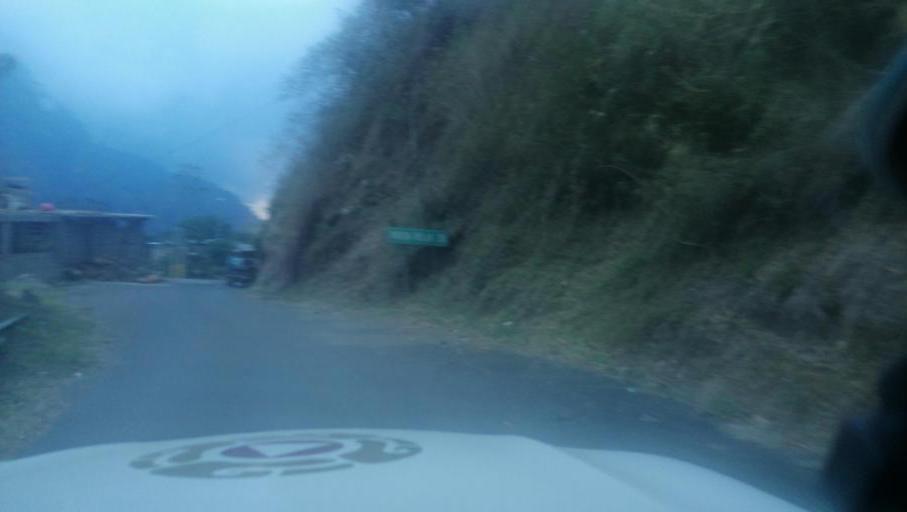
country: MX
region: Chiapas
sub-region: Cacahoatan
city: Benito Juarez
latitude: 15.1444
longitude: -92.1940
